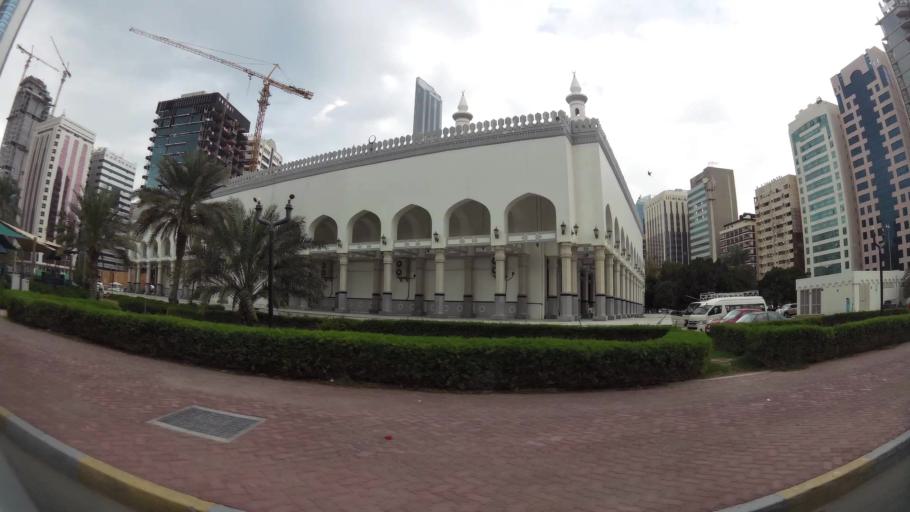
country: AE
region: Abu Dhabi
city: Abu Dhabi
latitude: 24.4840
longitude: 54.3527
